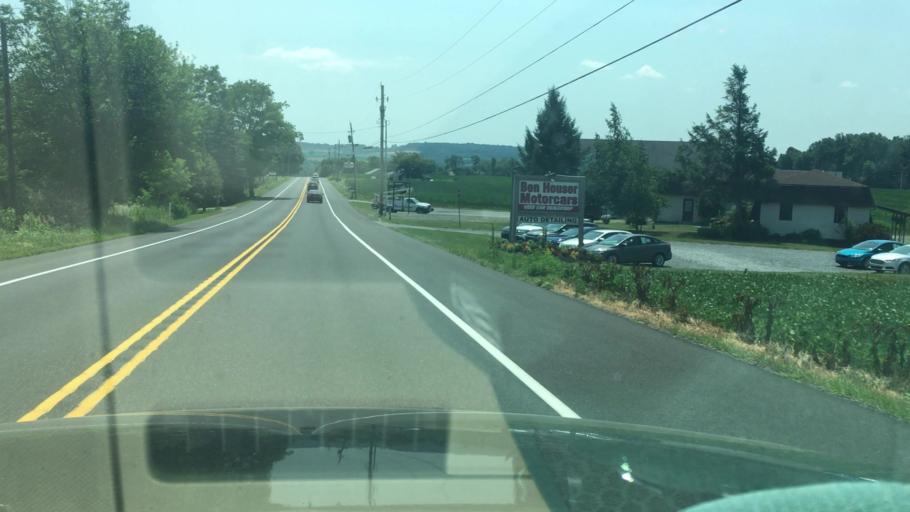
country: US
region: Pennsylvania
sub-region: Carbon County
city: Lehighton
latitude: 40.6963
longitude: -75.7526
